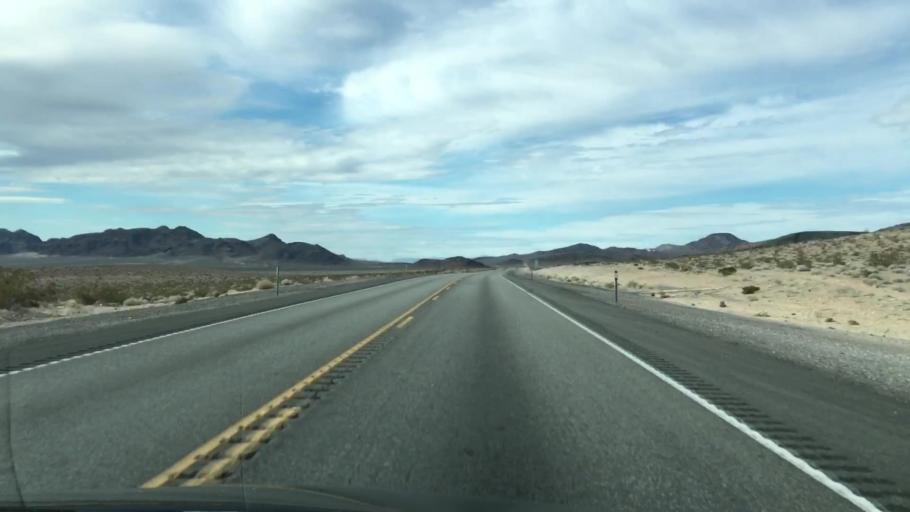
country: US
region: Nevada
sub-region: Nye County
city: Pahrump
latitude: 36.6124
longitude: -116.2749
